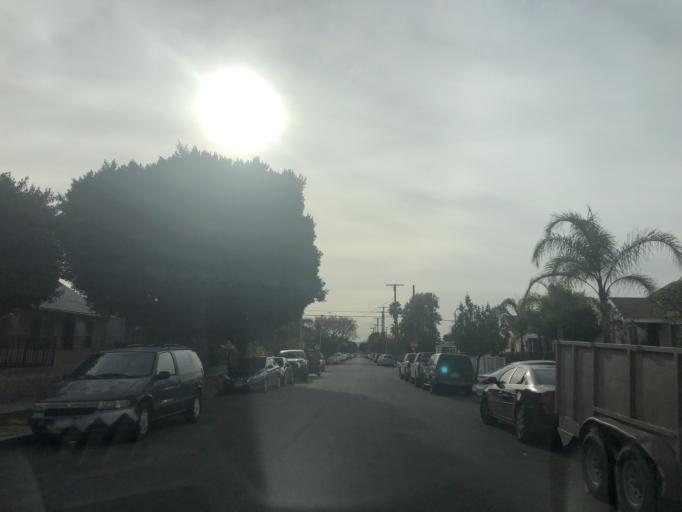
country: US
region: California
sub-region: Los Angeles County
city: San Fernando
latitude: 34.2666
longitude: -118.4305
